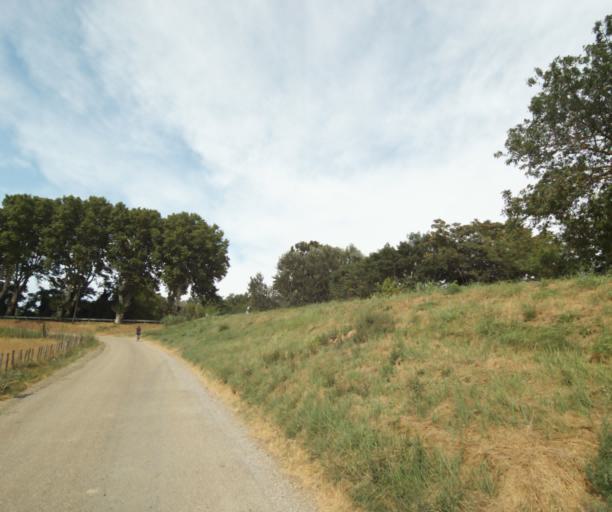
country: FR
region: Languedoc-Roussillon
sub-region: Departement de l'Herault
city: Marsillargues
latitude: 43.6388
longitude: 4.1897
